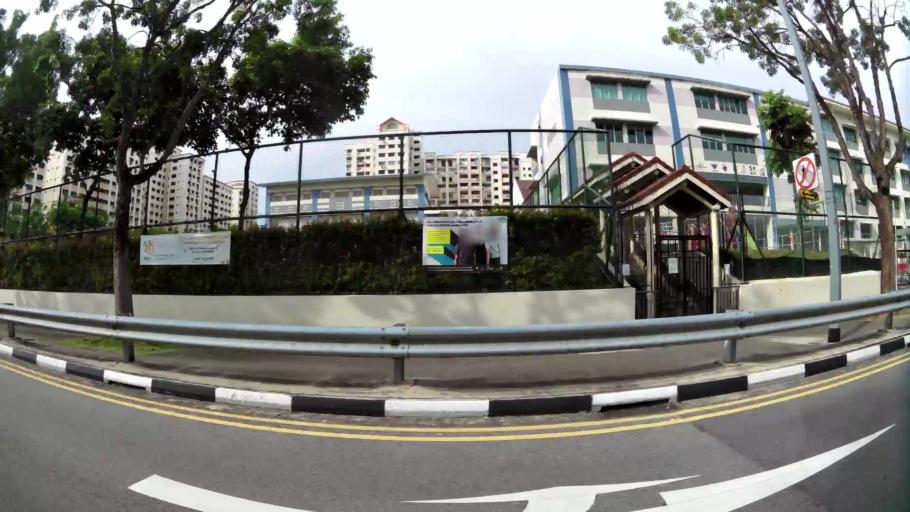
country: SG
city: Singapore
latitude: 1.3772
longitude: 103.8852
